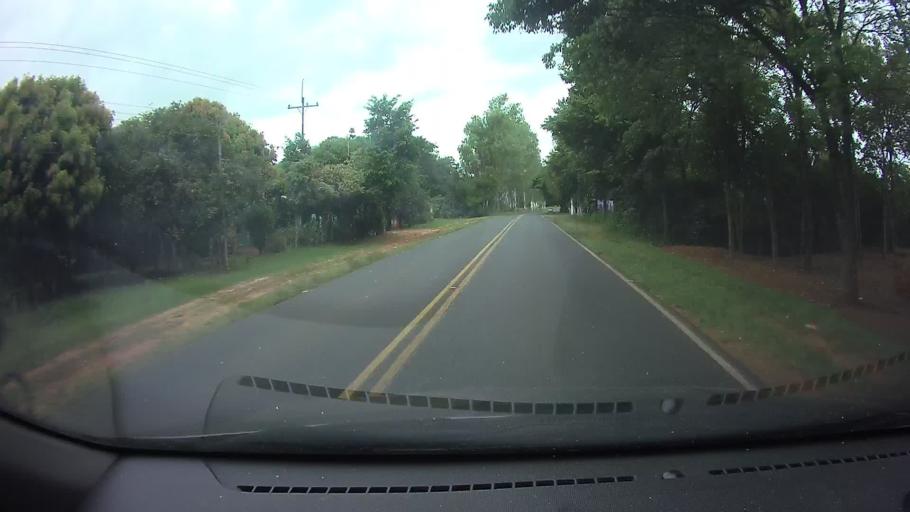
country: PY
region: Central
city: Nueva Italia
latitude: -25.5479
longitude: -57.4996
